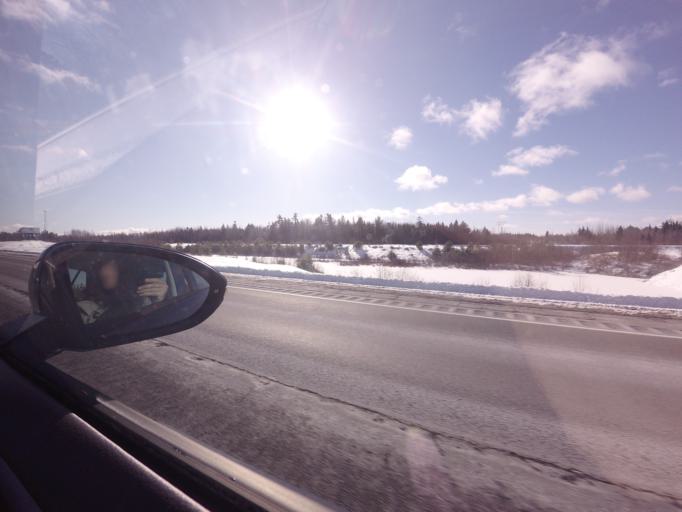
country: CA
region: New Brunswick
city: Fredericton
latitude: 45.8737
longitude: -66.6201
